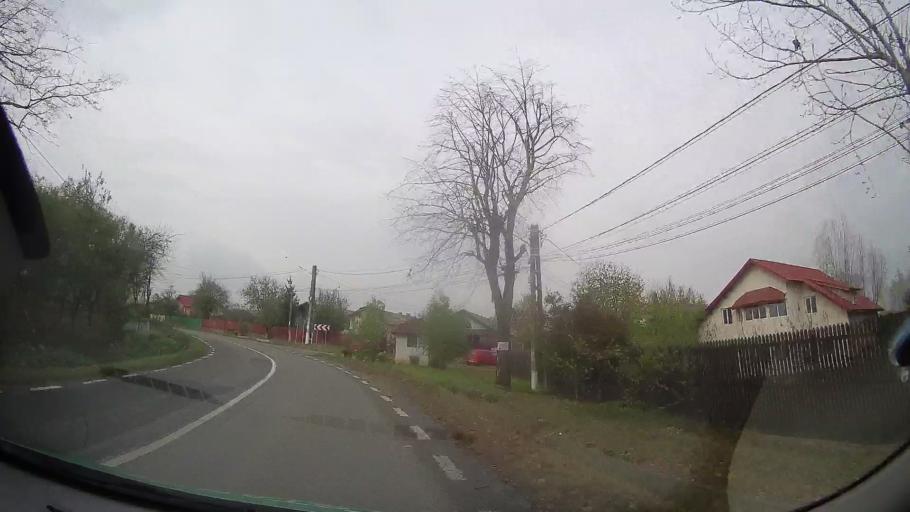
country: RO
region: Ilfov
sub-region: Comuna Gruiu
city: Gruiu
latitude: 44.7249
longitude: 26.2404
